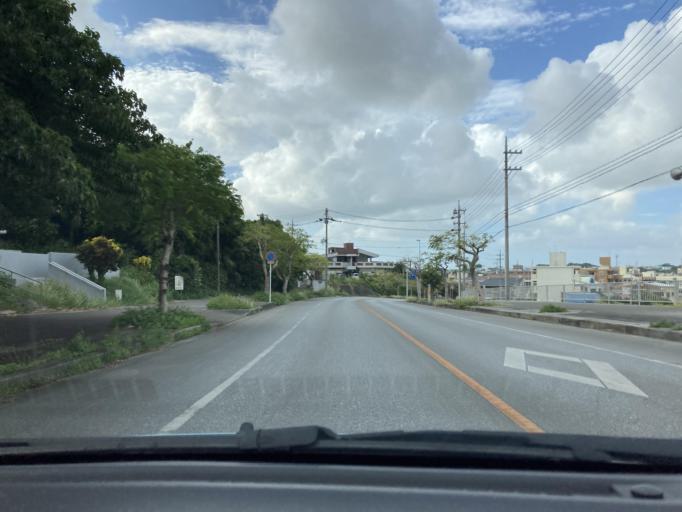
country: JP
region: Okinawa
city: Itoman
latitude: 26.1303
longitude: 127.6884
